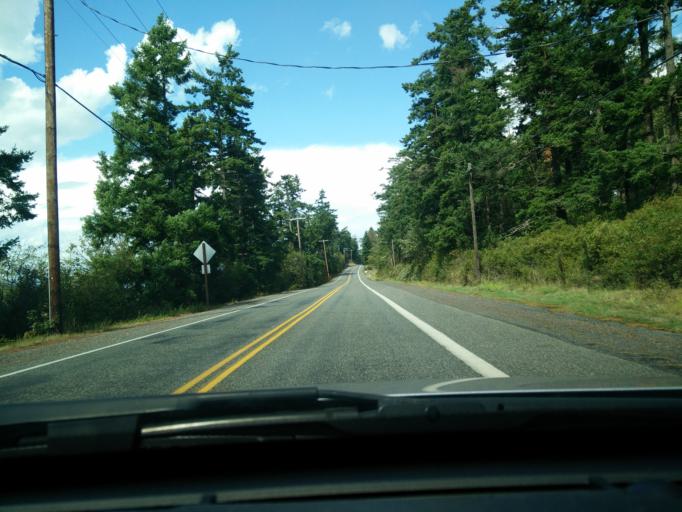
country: US
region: Washington
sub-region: Skagit County
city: Anacortes
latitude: 48.4885
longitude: -122.4808
